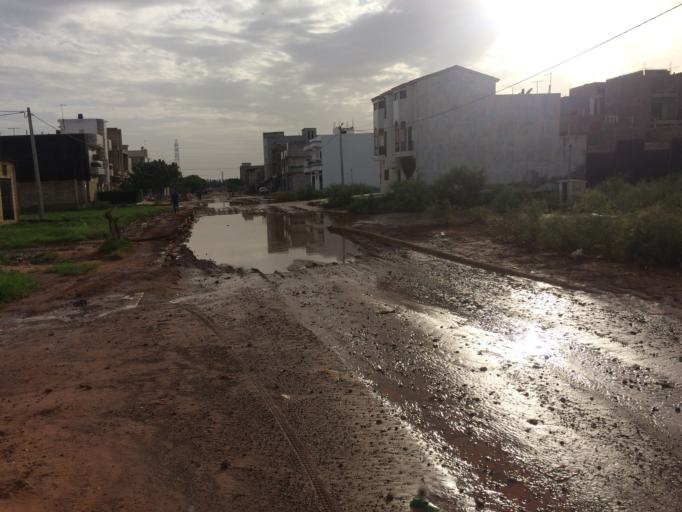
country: SN
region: Dakar
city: Pikine
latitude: 14.7435
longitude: -17.3039
